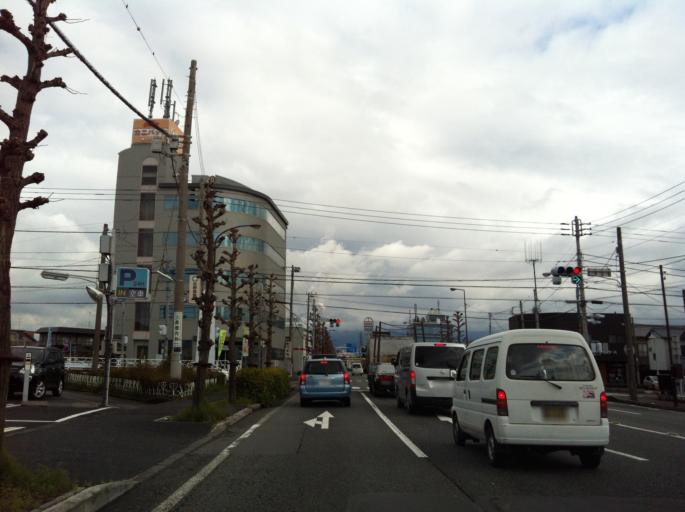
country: JP
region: Shizuoka
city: Fuji
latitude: 35.1437
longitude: 138.6623
